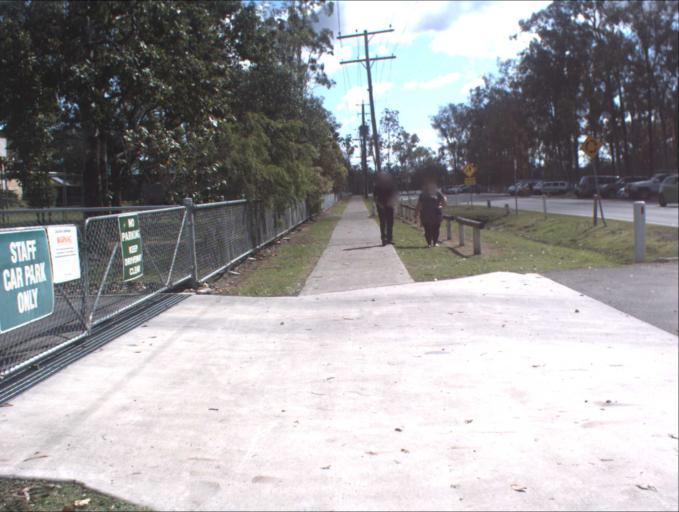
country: AU
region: Queensland
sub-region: Logan
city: Park Ridge South
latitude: -27.7120
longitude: 152.9774
